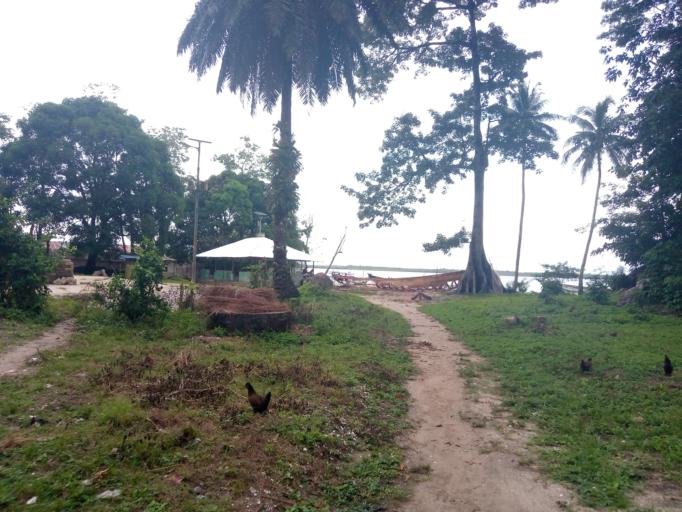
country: SL
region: Southern Province
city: Bonthe
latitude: 7.5219
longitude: -12.5008
